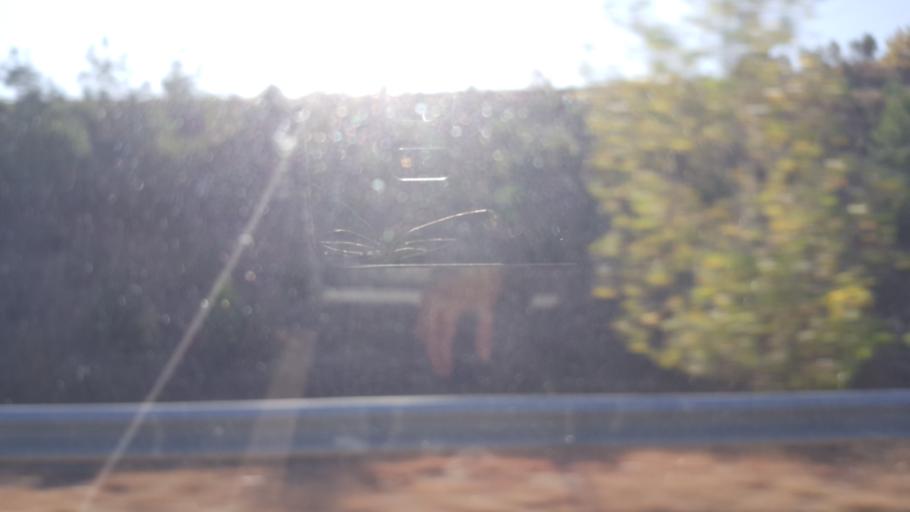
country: TR
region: Ankara
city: Cankaya
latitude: 39.8679
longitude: 32.9012
